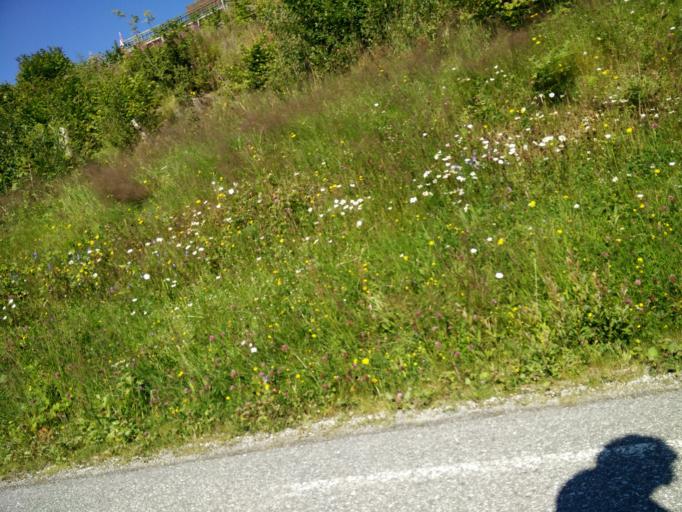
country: NO
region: More og Romsdal
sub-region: Kristiansund
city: Rensvik
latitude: 63.0223
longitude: 7.9499
